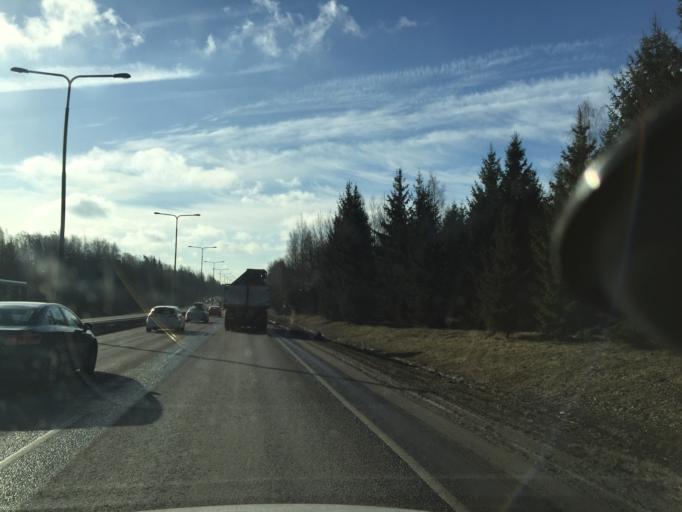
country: FI
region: Uusimaa
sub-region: Helsinki
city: Teekkarikylae
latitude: 60.2509
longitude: 24.8852
